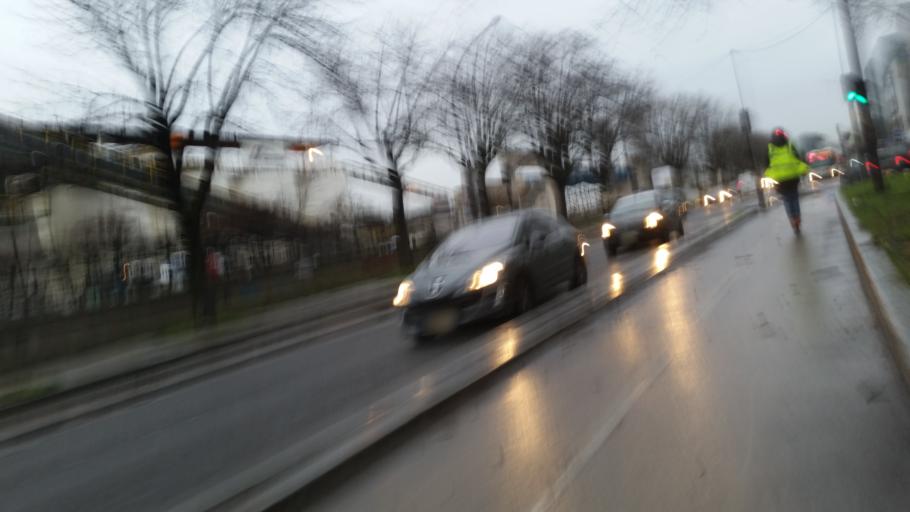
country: FR
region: Ile-de-France
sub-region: Departement du Val-de-Marne
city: Ivry-sur-Seine
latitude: 48.8254
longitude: 2.3883
